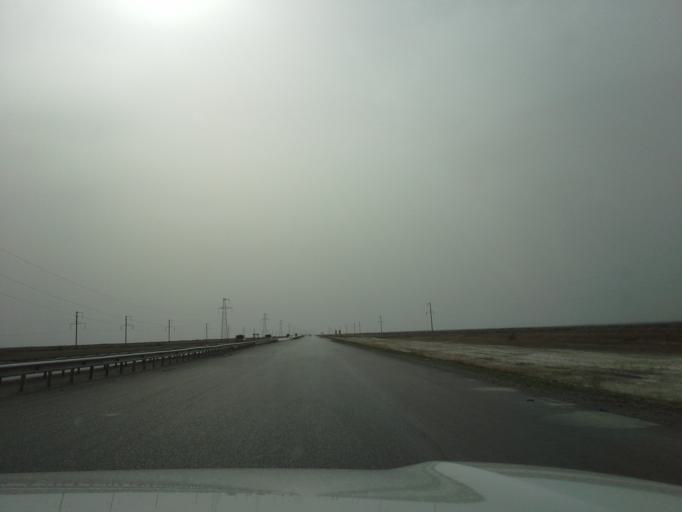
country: TM
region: Ahal
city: Kaka
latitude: 37.5317
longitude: 59.4132
